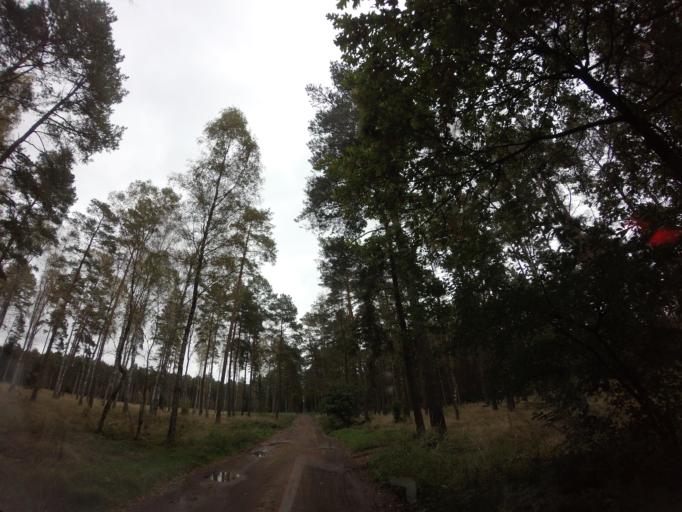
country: PL
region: West Pomeranian Voivodeship
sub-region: Powiat choszczenski
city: Drawno
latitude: 53.1419
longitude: 15.7078
